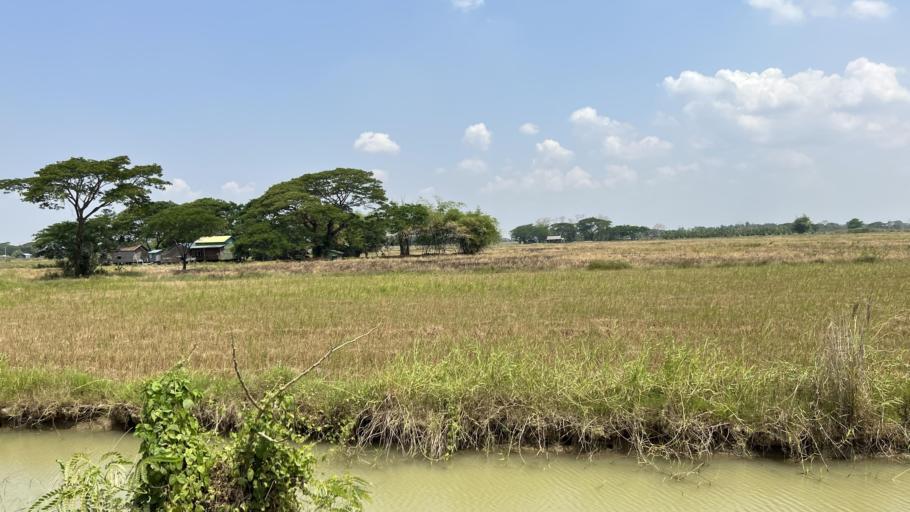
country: MM
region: Yangon
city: Kanbe
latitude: 16.7812
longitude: 95.9957
